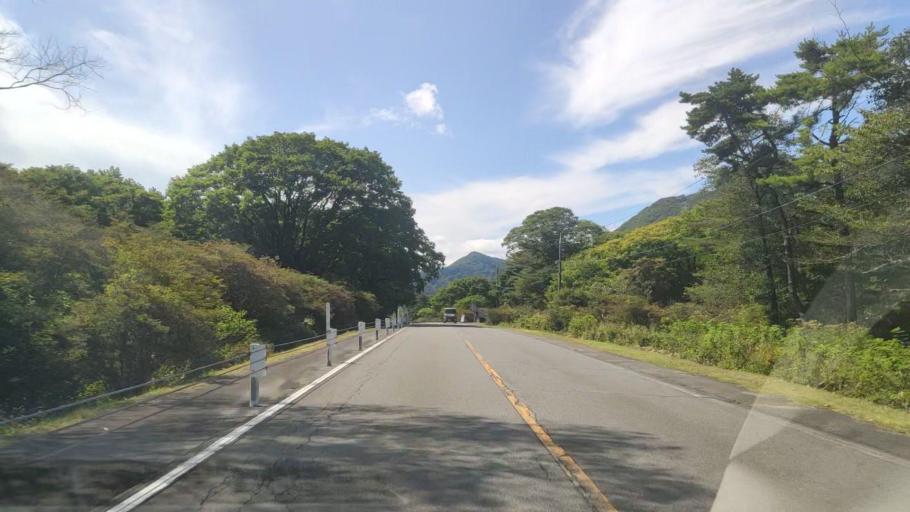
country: JP
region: Gunma
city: Shibukawa
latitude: 36.4805
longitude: 138.8950
